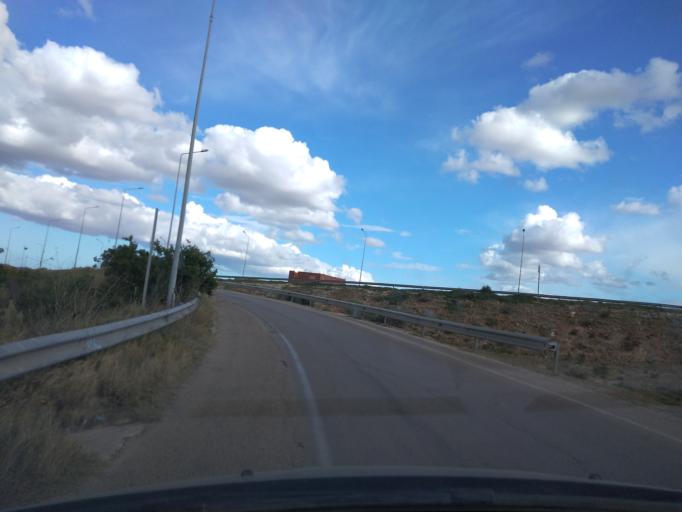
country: TN
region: Susah
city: Masakin
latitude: 35.7128
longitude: 10.5582
